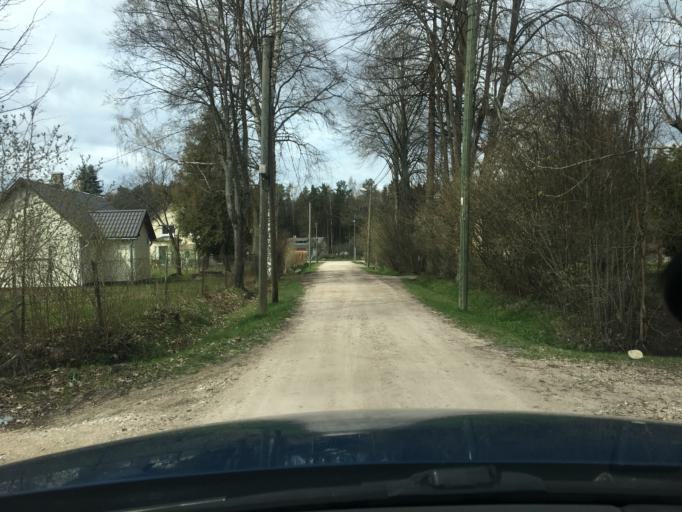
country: LV
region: Engure
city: Smarde
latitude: 56.9486
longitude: 23.4863
